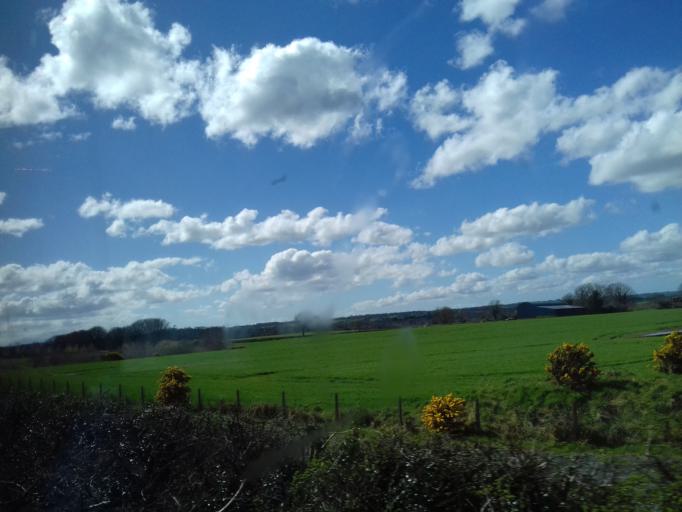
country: IE
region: Munster
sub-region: County Cork
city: Kanturk
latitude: 52.1022
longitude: -8.9550
